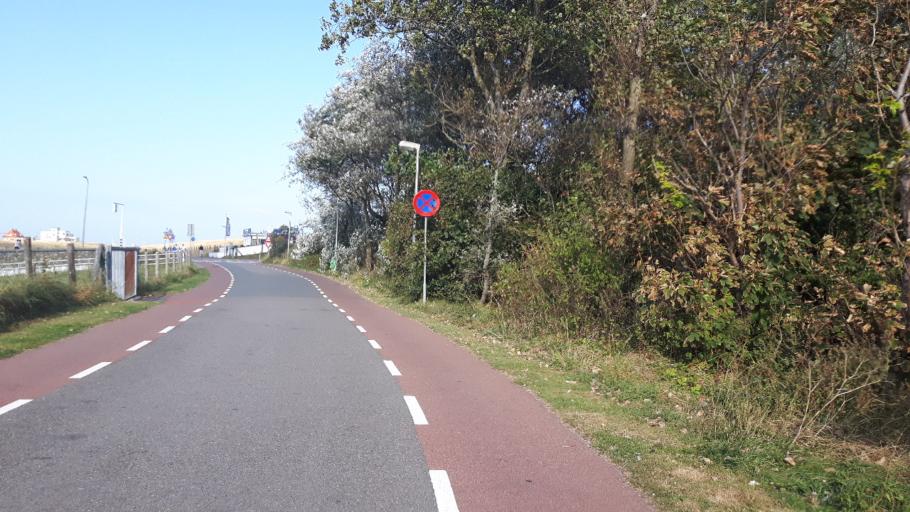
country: NL
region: South Holland
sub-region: Gemeente Katwijk
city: Katwijk aan Zee
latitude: 52.2082
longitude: 4.4080
